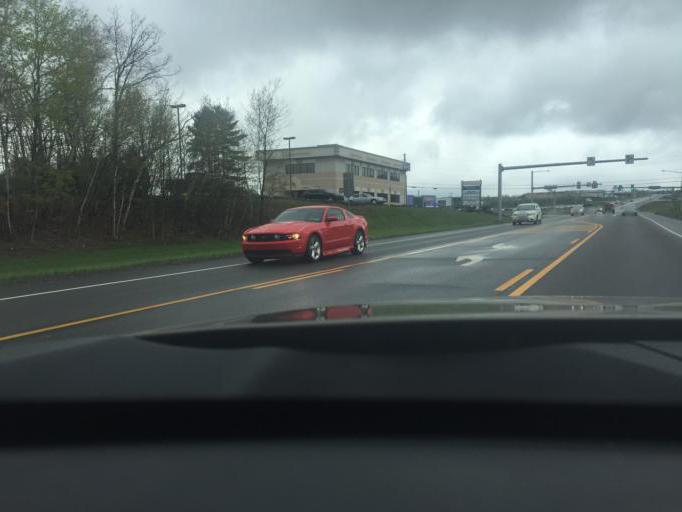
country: US
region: Pennsylvania
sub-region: Luzerne County
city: West Hazleton
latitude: 40.9902
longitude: -76.0053
